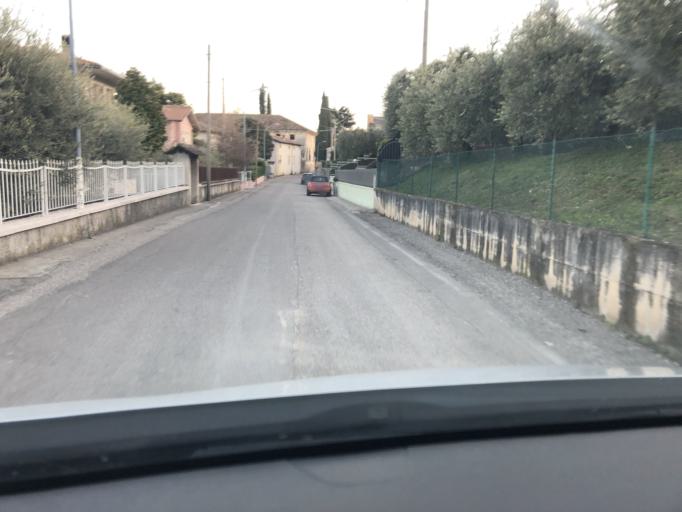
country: IT
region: Veneto
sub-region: Provincia di Verona
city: Sandra
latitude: 45.4558
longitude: 10.8155
